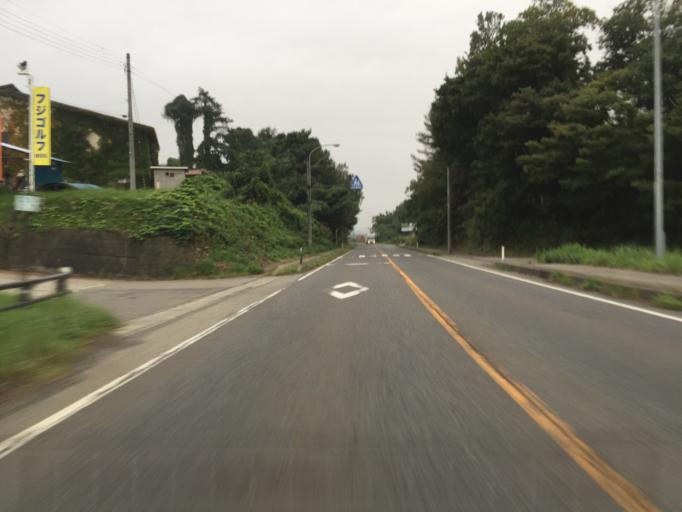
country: JP
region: Fukushima
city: Kitakata
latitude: 37.5398
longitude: 139.9445
